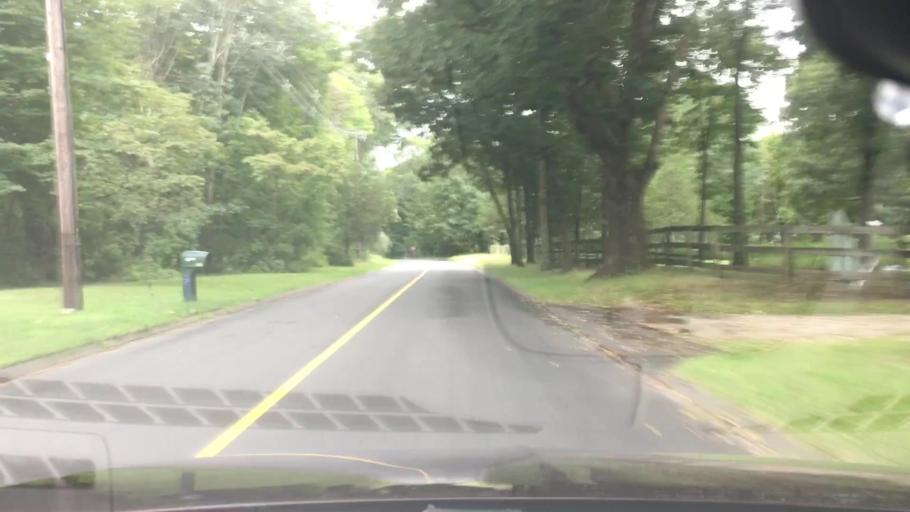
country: US
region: Connecticut
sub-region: New Haven County
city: Madison
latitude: 41.3271
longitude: -72.5915
